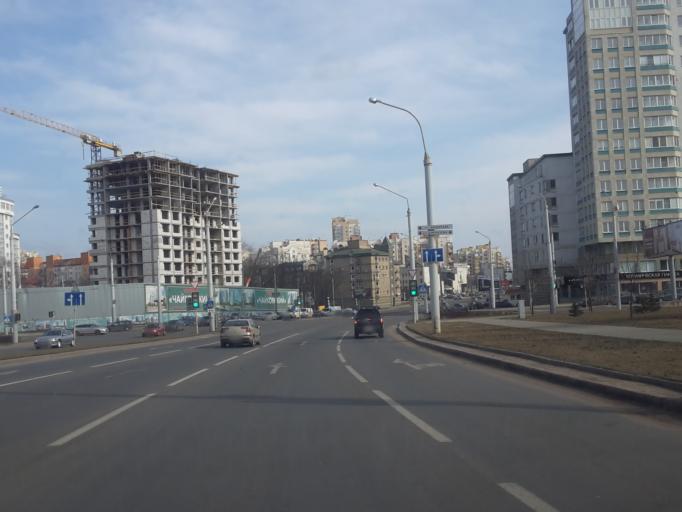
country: BY
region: Minsk
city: Minsk
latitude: 53.9105
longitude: 27.5256
